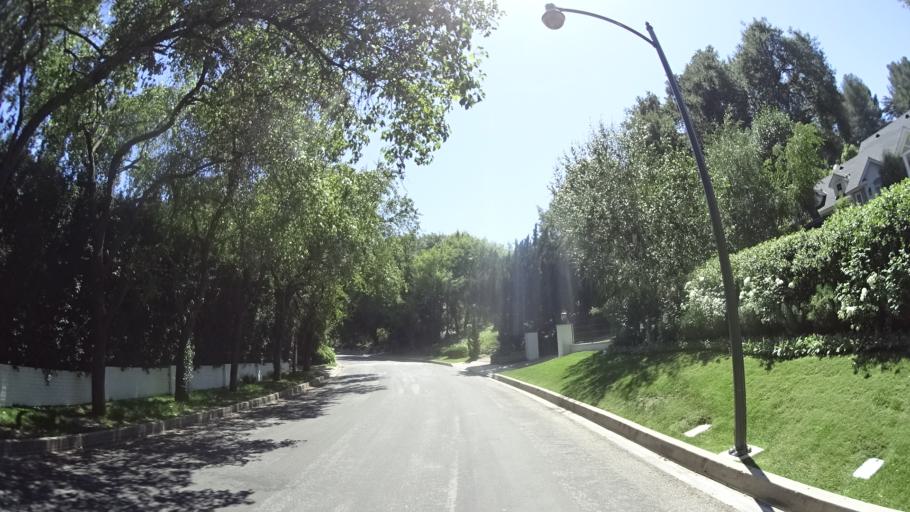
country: US
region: California
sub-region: Los Angeles County
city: Sherman Oaks
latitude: 34.1501
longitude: -118.4804
